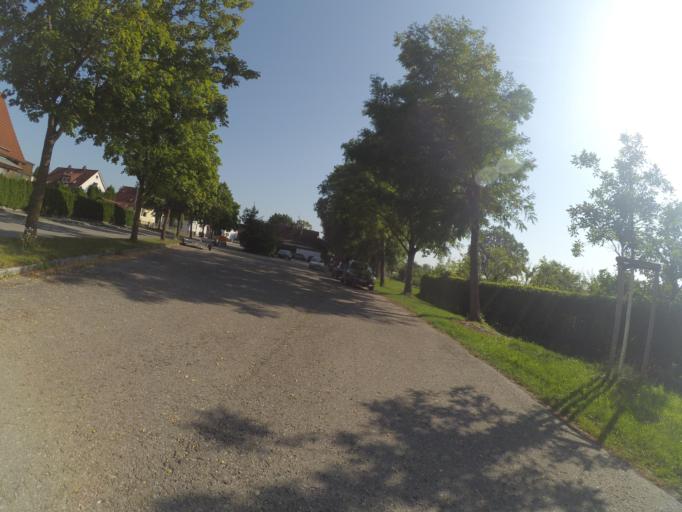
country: DE
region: Bavaria
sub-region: Swabia
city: Buchloe
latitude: 48.0440
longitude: 10.7258
